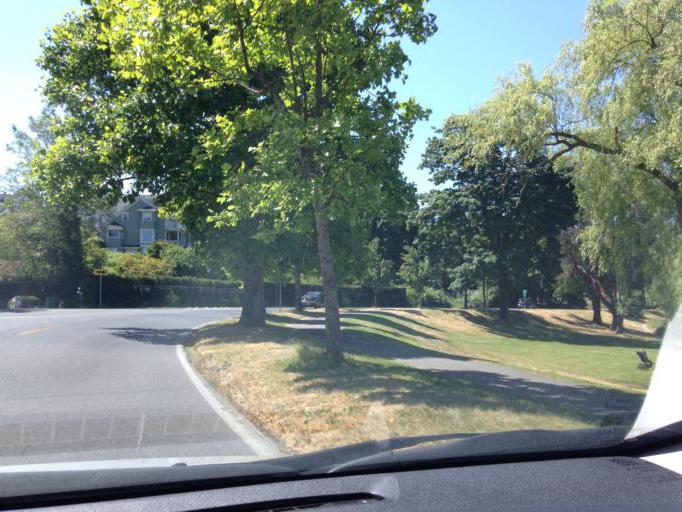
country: US
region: Washington
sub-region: King County
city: Mercer Island
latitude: 47.5701
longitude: -122.2791
